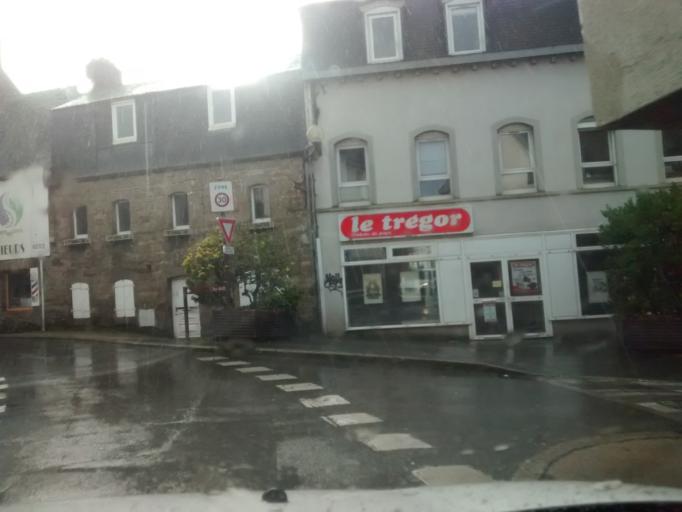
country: FR
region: Brittany
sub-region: Departement des Cotes-d'Armor
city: Lannion
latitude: 48.7325
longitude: -3.4565
